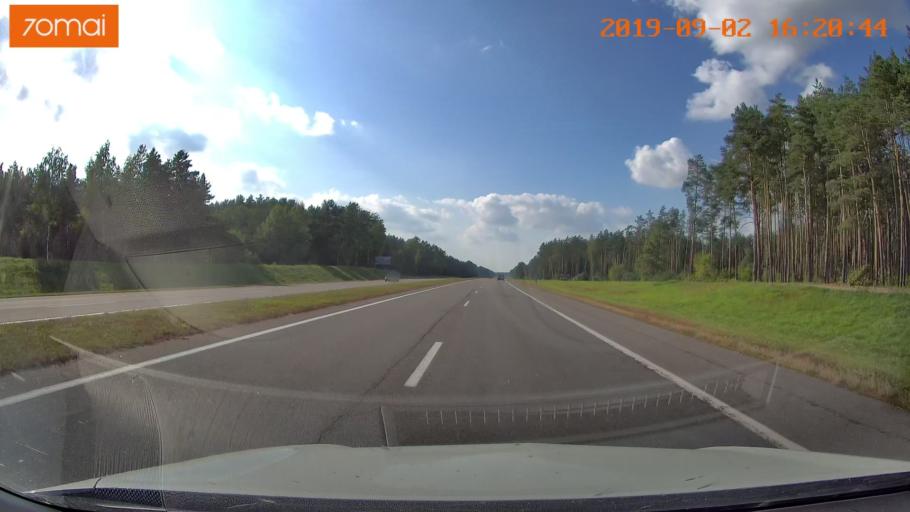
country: BY
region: Minsk
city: Chervyen'
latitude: 53.7251
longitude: 28.3713
